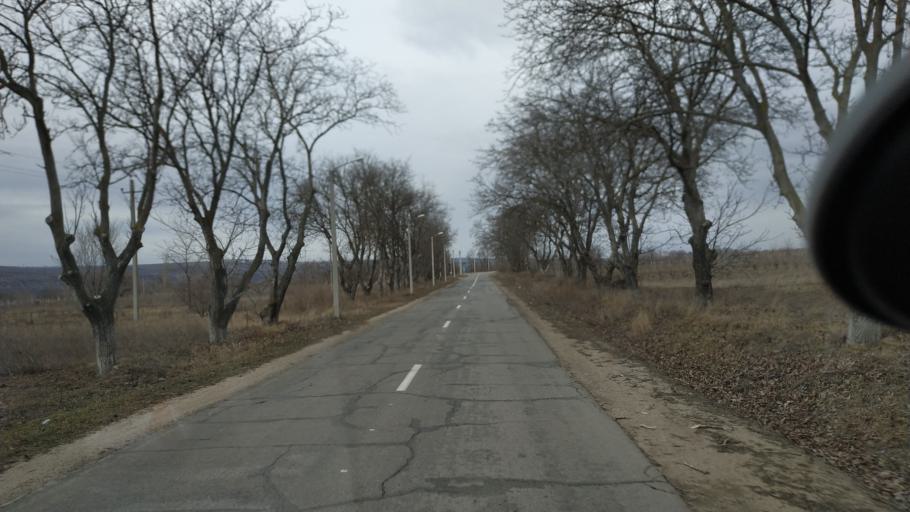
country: MD
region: Telenesti
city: Cocieri
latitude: 47.3227
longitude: 29.0986
